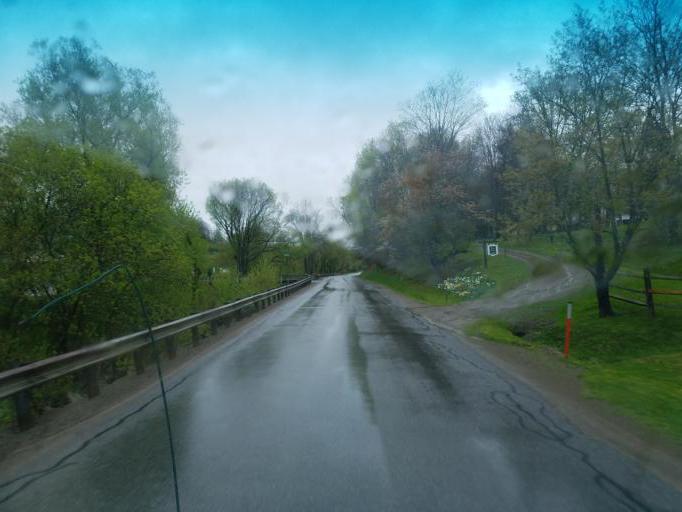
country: US
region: Pennsylvania
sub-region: Tioga County
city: Westfield
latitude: 41.9538
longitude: -77.6476
